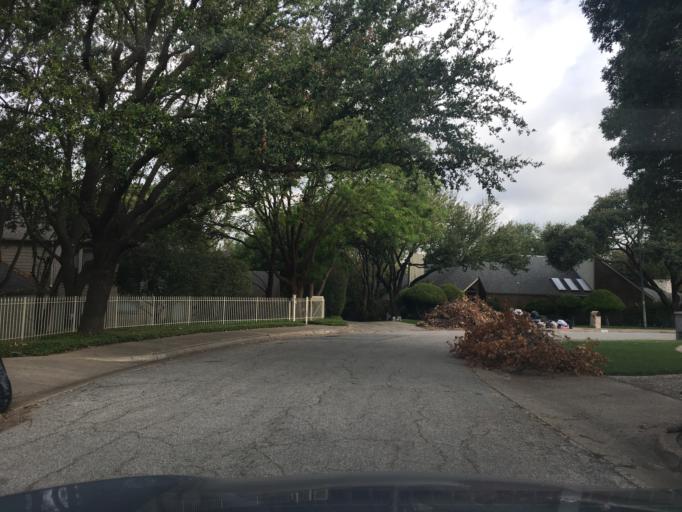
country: US
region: Texas
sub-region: Dallas County
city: Richardson
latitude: 32.9005
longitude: -96.7490
